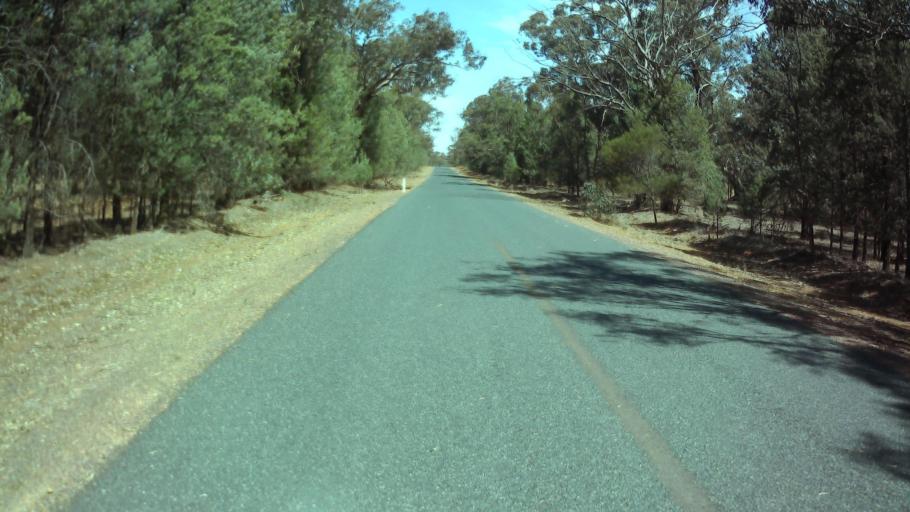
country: AU
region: New South Wales
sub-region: Weddin
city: Grenfell
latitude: -34.0715
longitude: 148.1404
